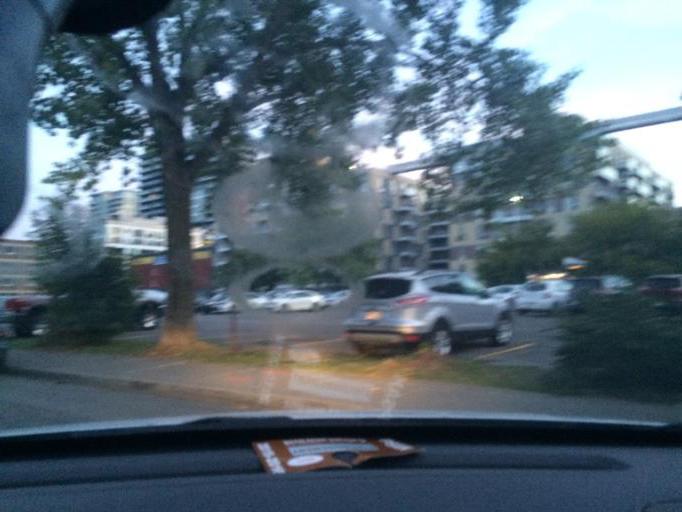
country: CA
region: Quebec
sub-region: Montreal
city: Montreal
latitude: 45.4964
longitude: -73.5598
